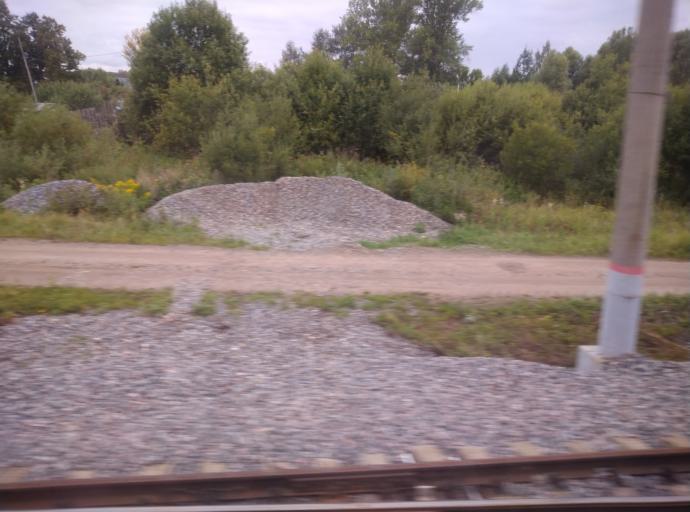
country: RU
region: Kostroma
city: Kosmynino
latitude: 57.5864
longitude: 40.7585
